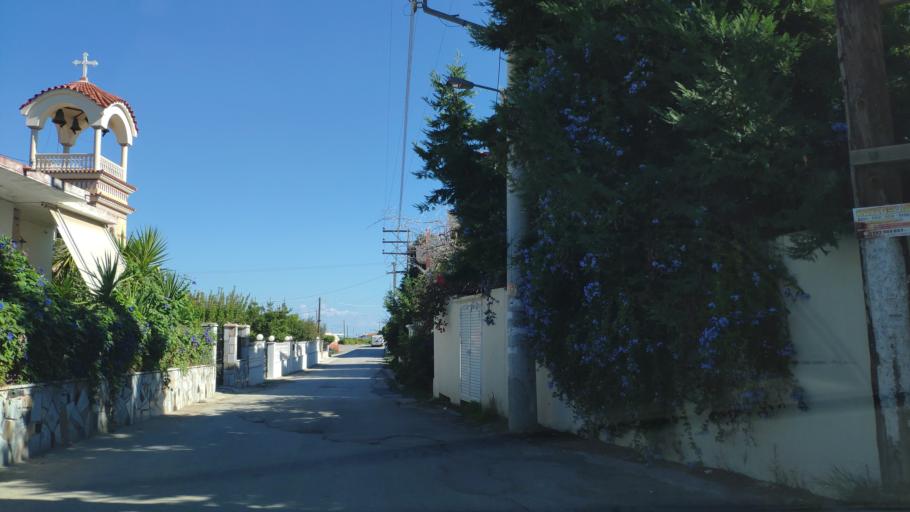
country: GR
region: Peloponnese
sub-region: Nomos Korinthias
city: Loutra Oraias Elenis
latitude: 37.8468
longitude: 22.9996
